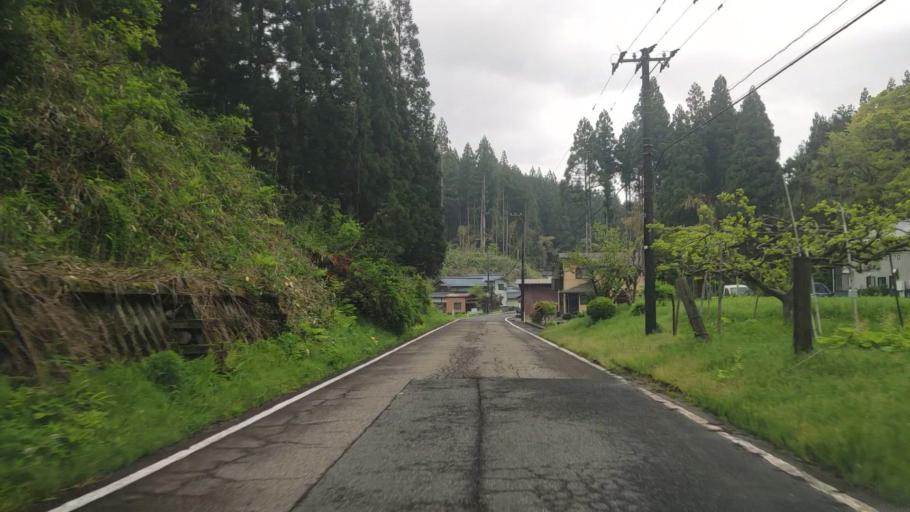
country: JP
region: Niigata
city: Gosen
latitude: 37.7201
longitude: 139.1271
